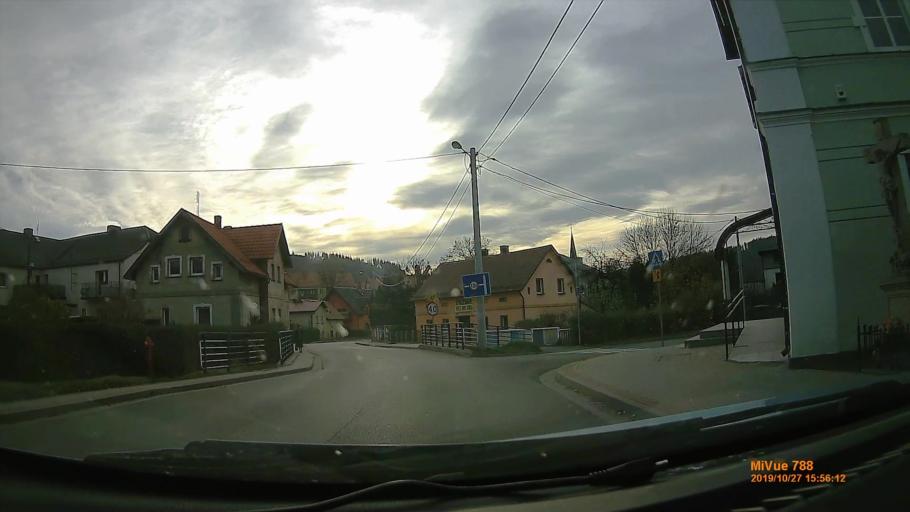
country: PL
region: Lower Silesian Voivodeship
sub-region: Powiat klodzki
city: Bozkow
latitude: 50.5457
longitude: 16.5510
